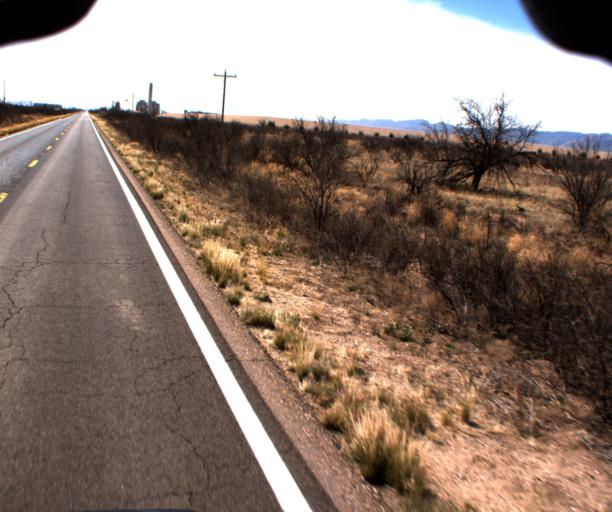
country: US
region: Arizona
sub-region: Cochise County
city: Willcox
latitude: 32.0827
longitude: -109.9025
